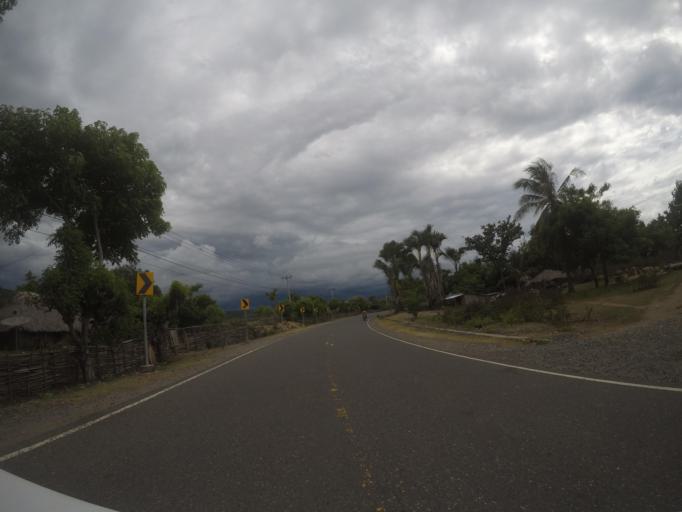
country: TL
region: Liquica
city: Maubara
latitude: -8.7553
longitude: 125.1009
